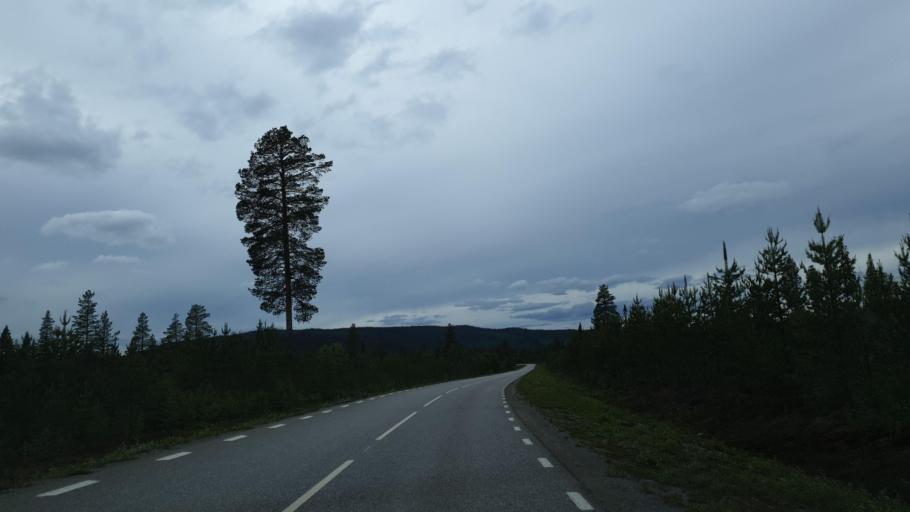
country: SE
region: Vaesterbotten
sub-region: Sorsele Kommun
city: Sorsele
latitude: 65.5440
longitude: 17.4372
